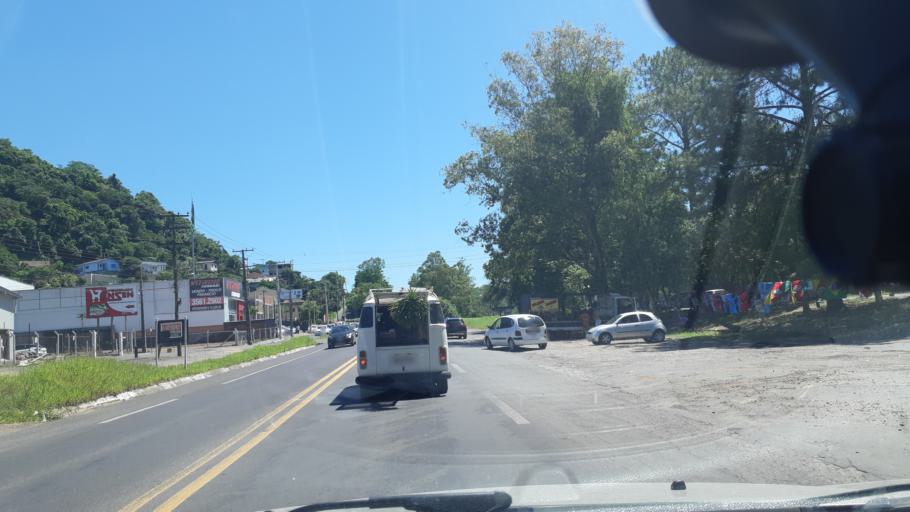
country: BR
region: Rio Grande do Sul
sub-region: Estancia Velha
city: Estancia Velha
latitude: -29.6464
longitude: -51.1435
